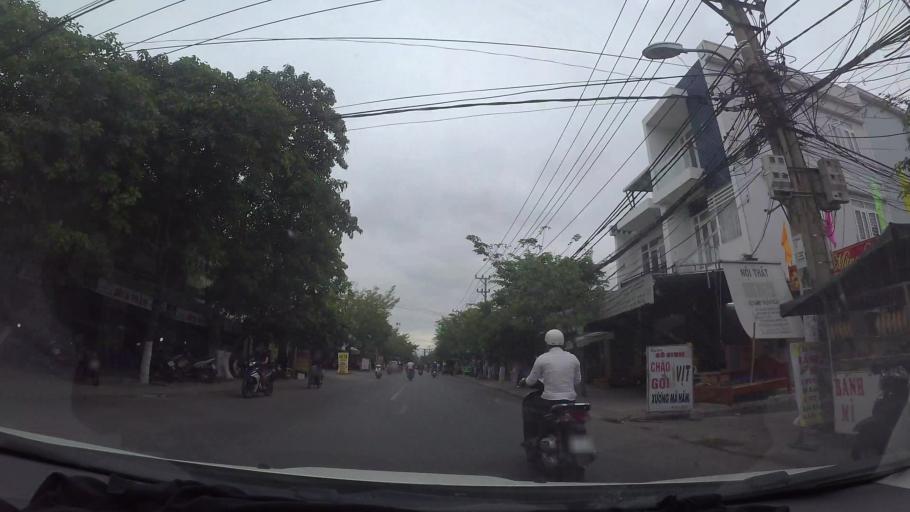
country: VN
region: Da Nang
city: Lien Chieu
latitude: 16.0708
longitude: 108.1438
